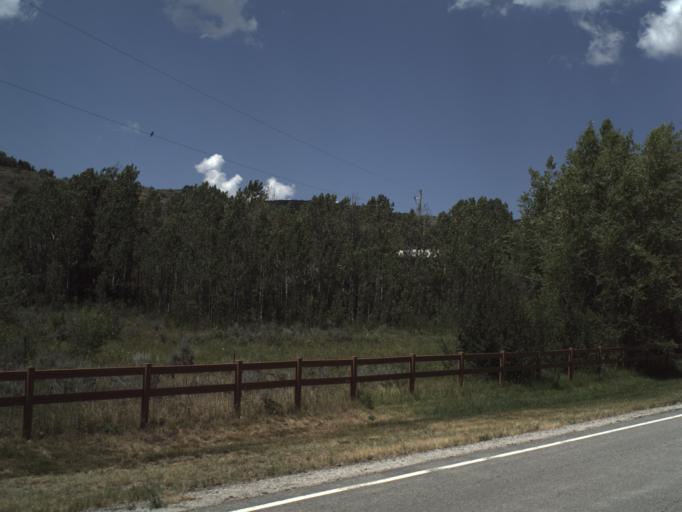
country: US
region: Utah
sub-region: Weber County
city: Wolf Creek
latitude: 41.3074
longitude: -111.6166
